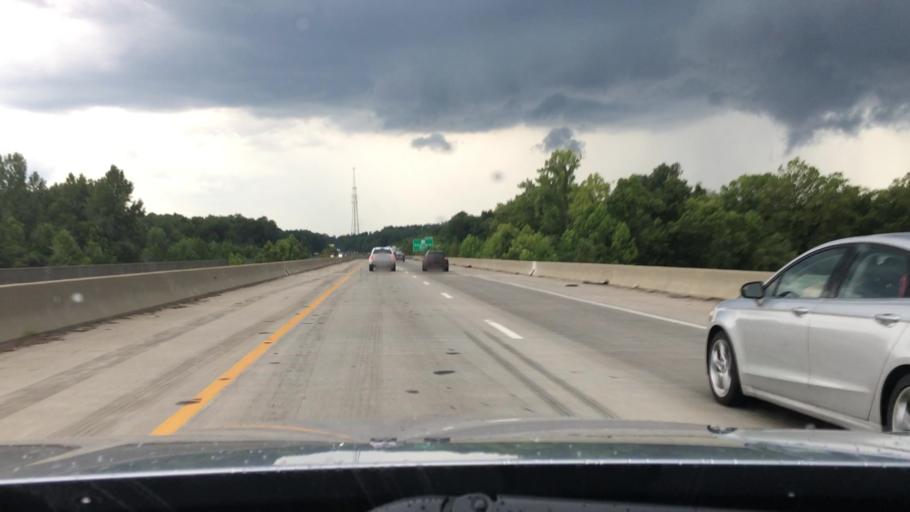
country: US
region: North Carolina
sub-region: Halifax County
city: Weldon
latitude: 36.4508
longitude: -77.6205
